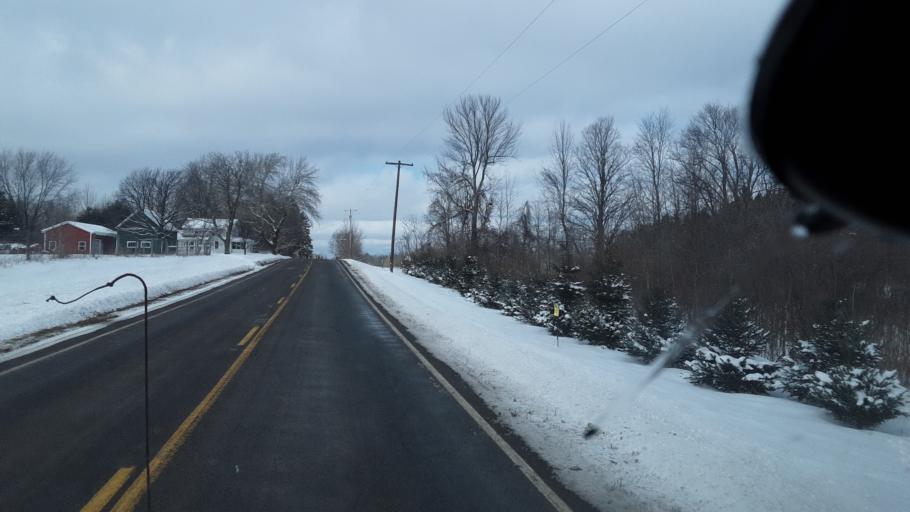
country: US
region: New York
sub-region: Wayne County
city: Lyons
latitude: 43.0951
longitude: -77.0422
